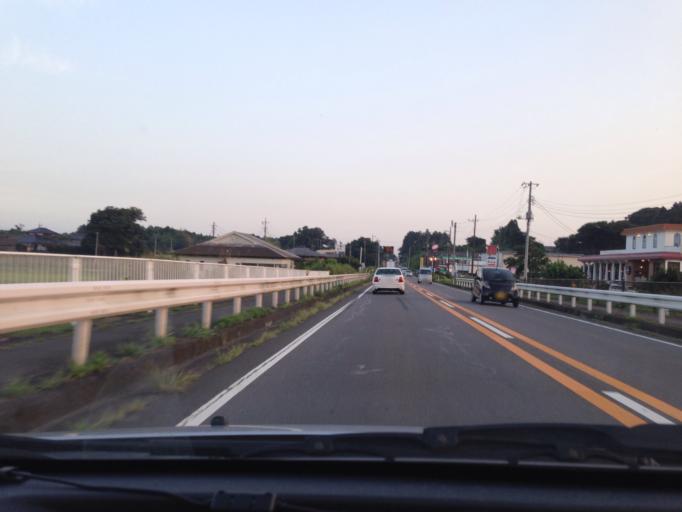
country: JP
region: Ibaraki
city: Ishioka
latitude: 36.1493
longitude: 140.2386
